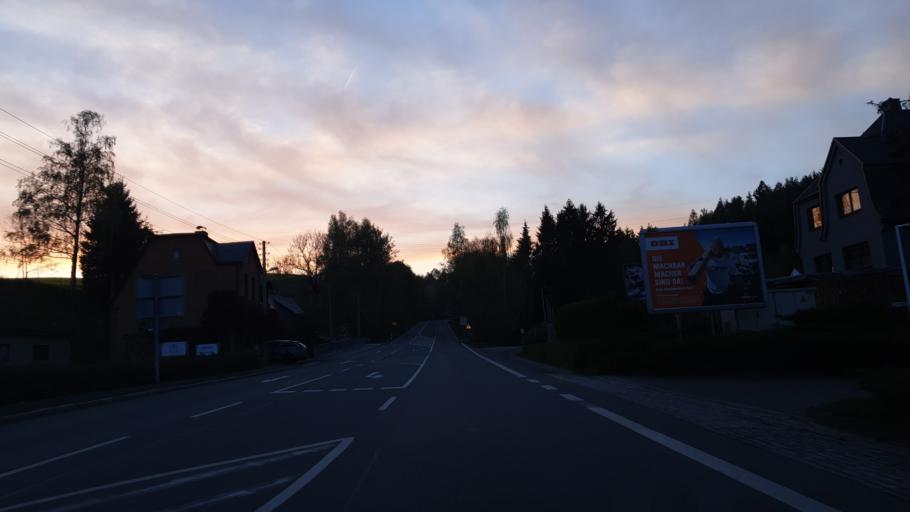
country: DE
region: Saxony
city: Lossnitz
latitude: 50.6313
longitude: 12.7367
